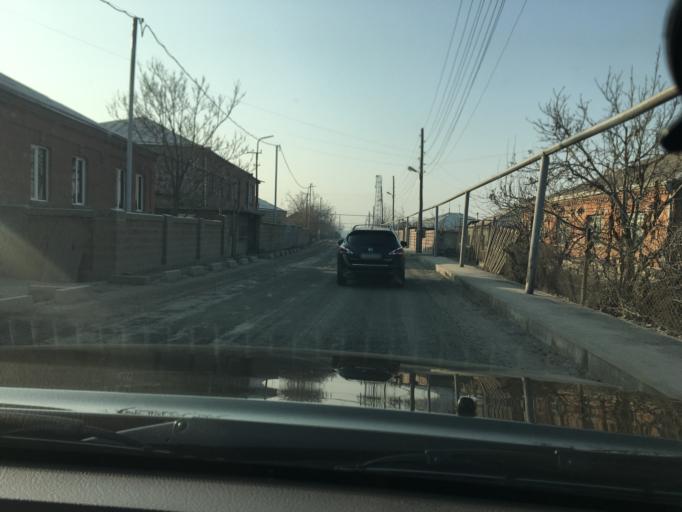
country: AM
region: Armavir
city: Janfida
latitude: 40.0477
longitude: 44.0305
